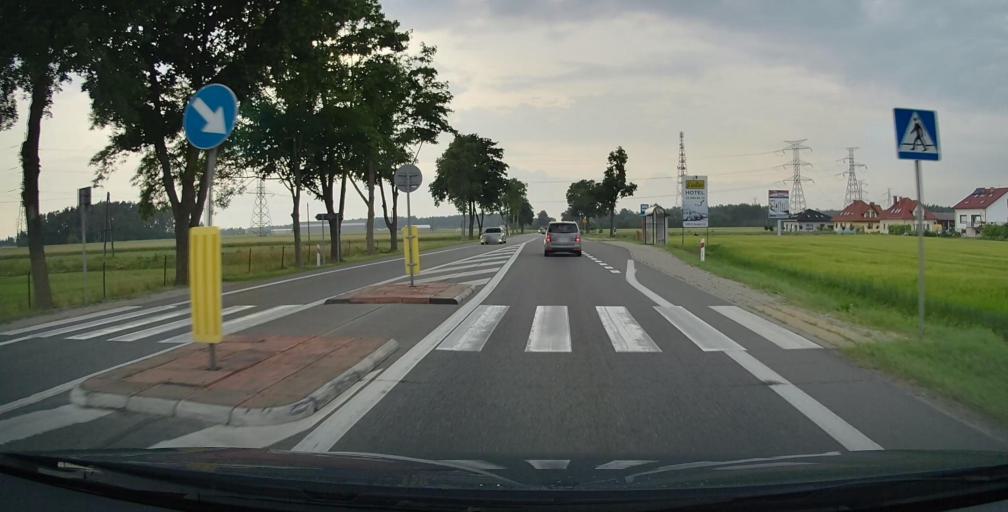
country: PL
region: Masovian Voivodeship
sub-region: Powiat siedlecki
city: Zbuczyn
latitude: 52.1181
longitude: 22.3628
